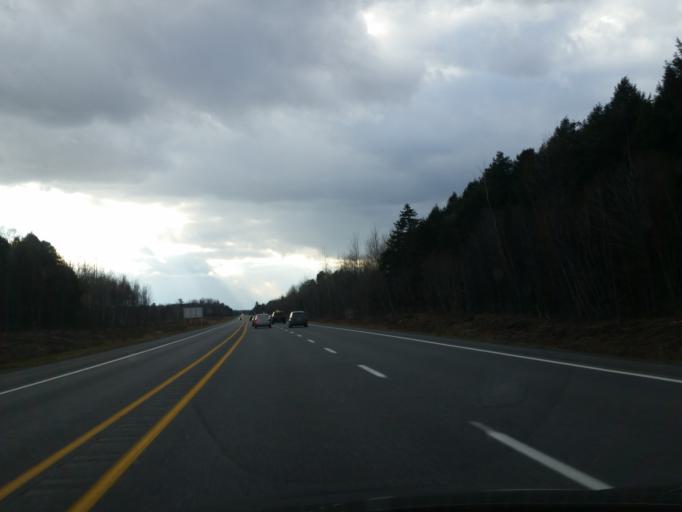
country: CA
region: Quebec
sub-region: Laurentides
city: Saint-Colomban
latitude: 45.6647
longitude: -74.2052
